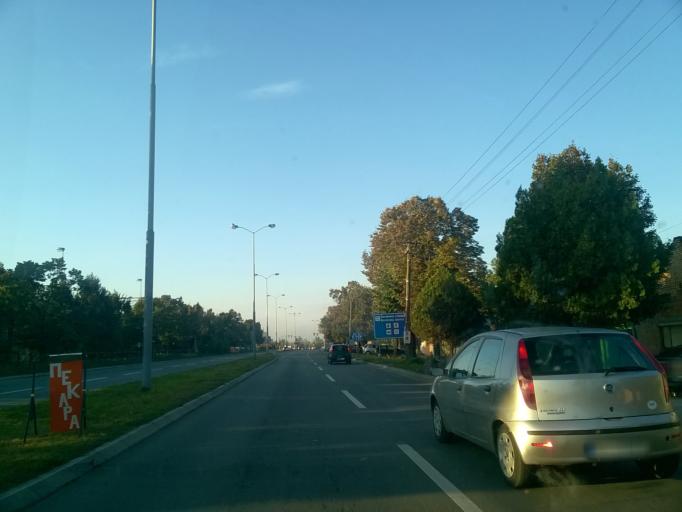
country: RS
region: Autonomna Pokrajina Vojvodina
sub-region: Juznobanatski Okrug
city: Pancevo
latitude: 44.8597
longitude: 20.6554
